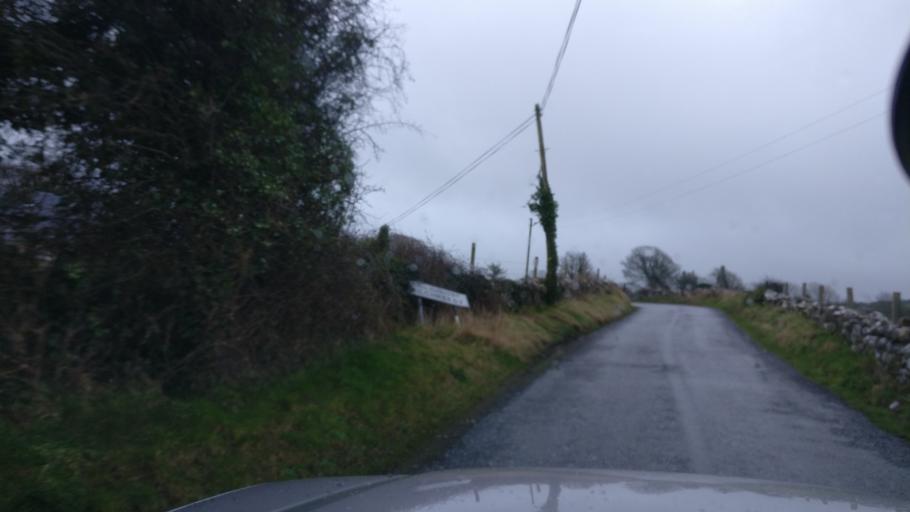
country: IE
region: Connaught
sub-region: County Galway
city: Loughrea
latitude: 53.1800
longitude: -8.6553
